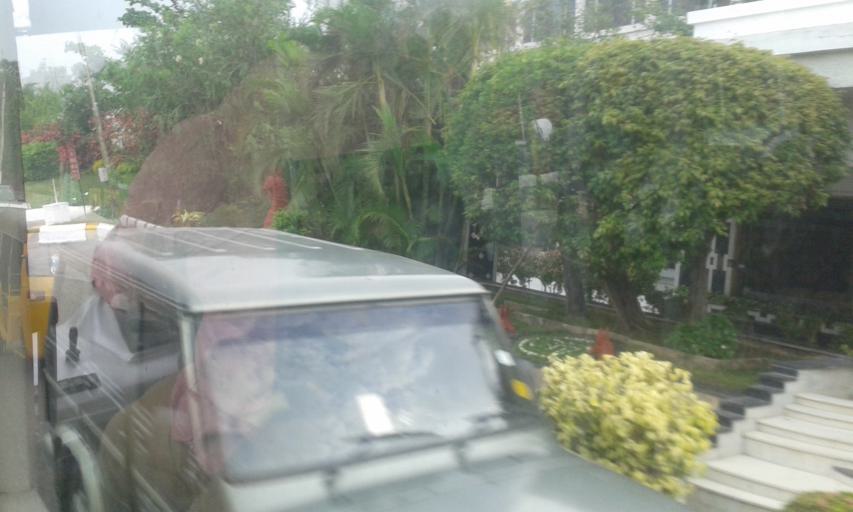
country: IN
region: Tamil Nadu
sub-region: Kancheepuram
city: Guduvancheri
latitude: 12.8238
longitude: 80.0412
